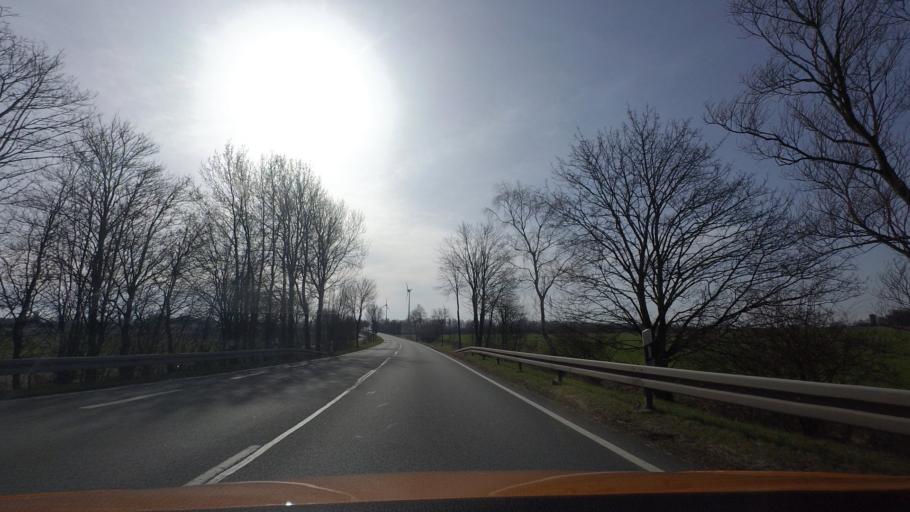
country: DE
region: Lower Saxony
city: Uchte
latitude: 52.4869
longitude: 8.8901
